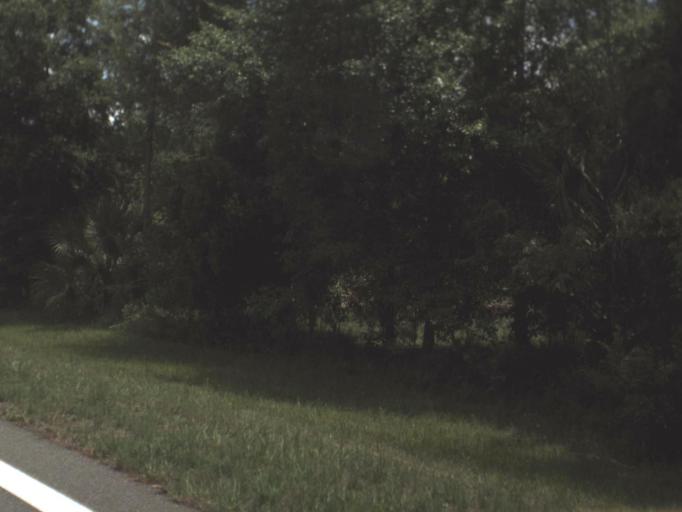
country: US
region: Florida
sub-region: Levy County
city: Chiefland
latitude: 29.2504
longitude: -82.9062
